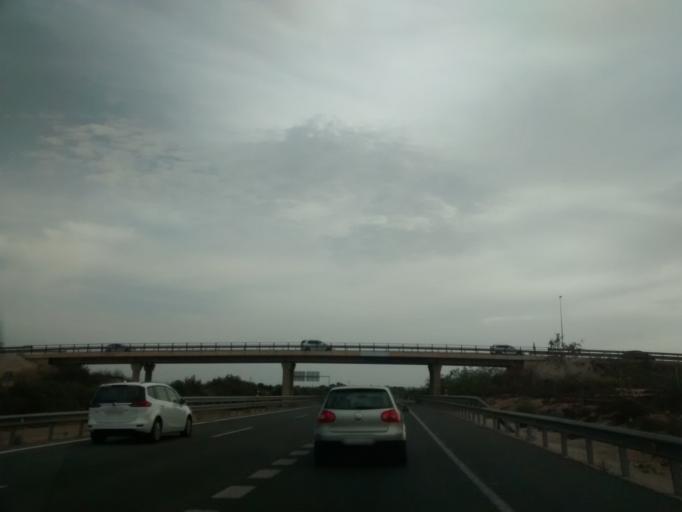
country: ES
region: Valencia
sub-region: Provincia de Alicante
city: Pilar de la Horadada
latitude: 37.8946
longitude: -0.7688
